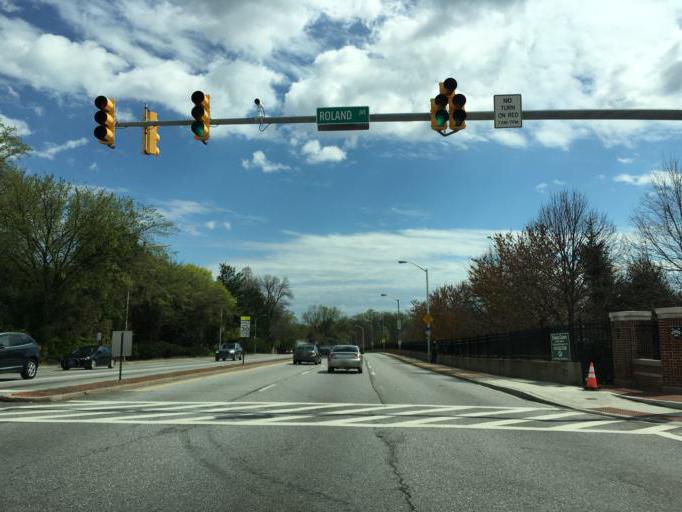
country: US
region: Maryland
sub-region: Baltimore County
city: Towson
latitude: 39.3621
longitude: -76.6348
